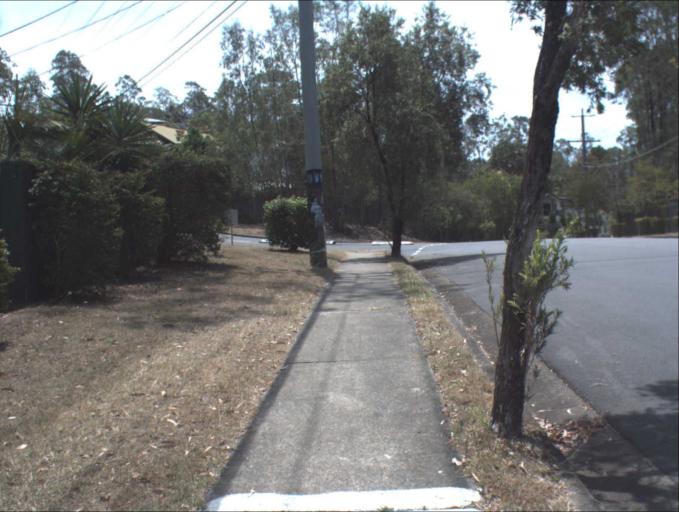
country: AU
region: Queensland
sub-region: Logan
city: Beenleigh
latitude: -27.6662
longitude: 153.1981
